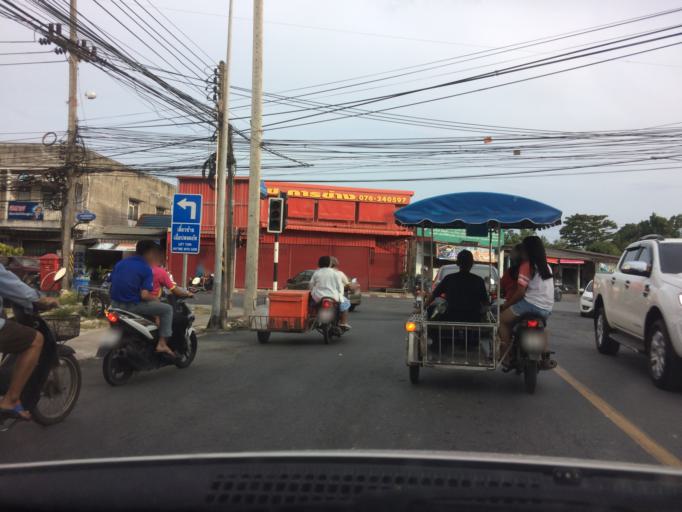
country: TH
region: Phuket
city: Ban Talat Yai
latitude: 7.8854
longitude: 98.4039
